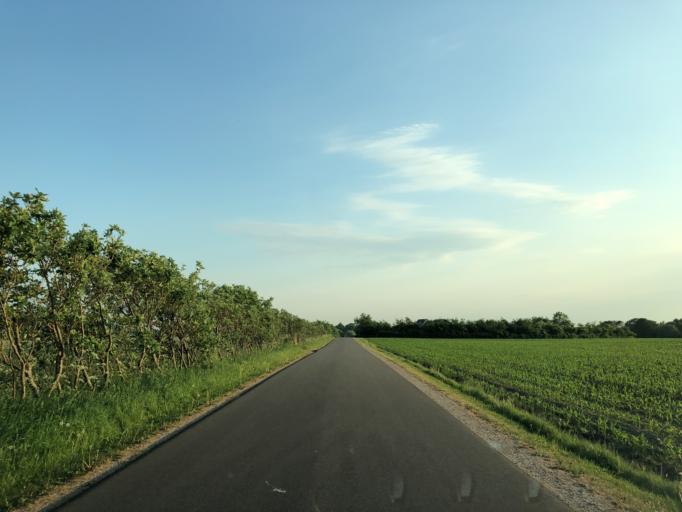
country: DK
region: Central Jutland
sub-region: Struer Kommune
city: Struer
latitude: 56.4281
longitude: 8.5037
